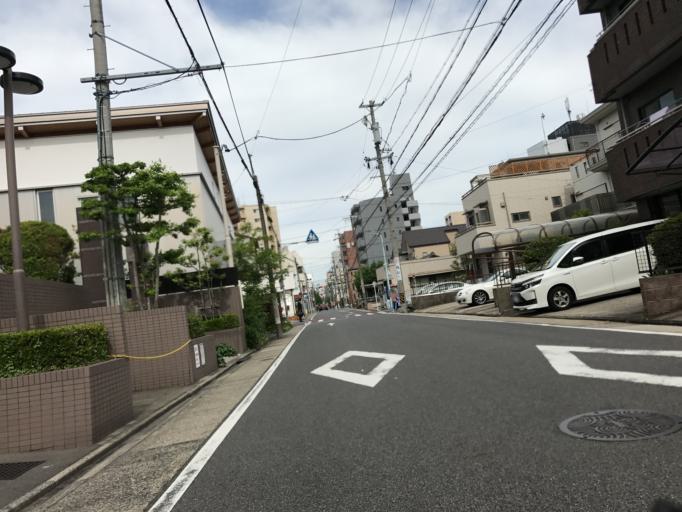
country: JP
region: Aichi
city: Nagoya-shi
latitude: 35.1668
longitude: 136.9430
